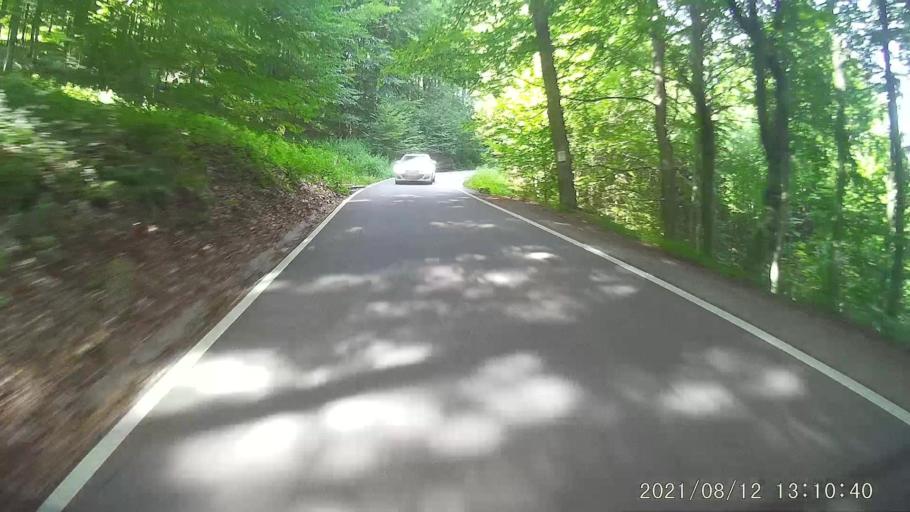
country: PL
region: Lower Silesian Voivodeship
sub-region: Powiat klodzki
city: Stronie Slaskie
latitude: 50.2460
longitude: 16.8493
